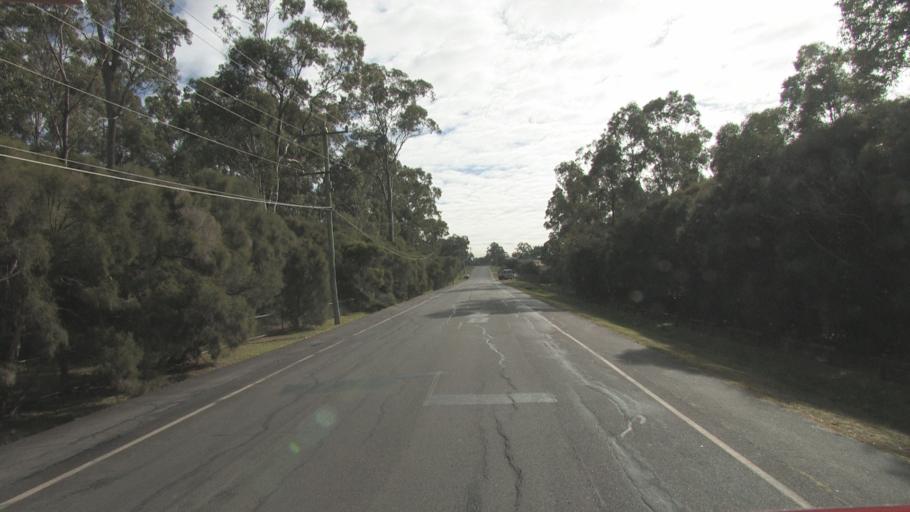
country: AU
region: Queensland
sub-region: Logan
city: Waterford West
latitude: -27.6886
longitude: 153.1120
